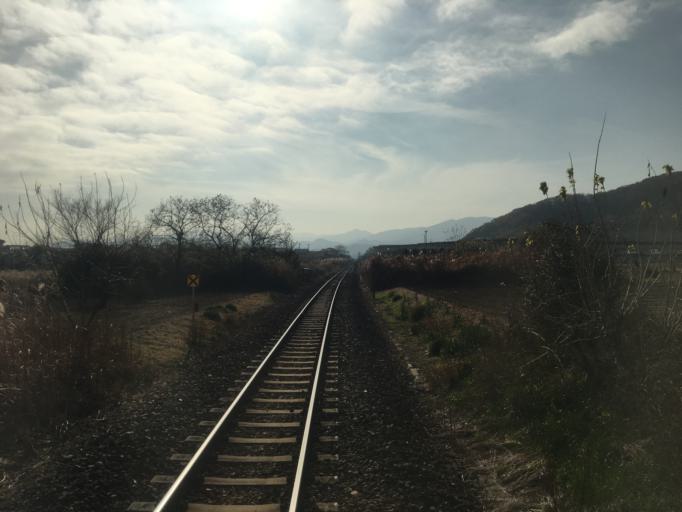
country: JP
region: Saitama
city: Yorii
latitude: 36.1337
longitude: 139.2063
